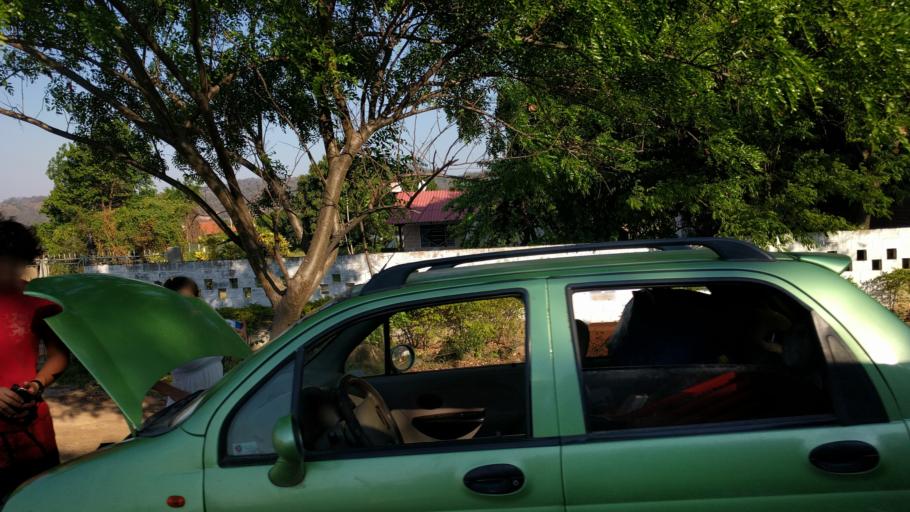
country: BO
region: Santa Cruz
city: Jorochito
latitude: -18.1410
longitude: -63.4791
